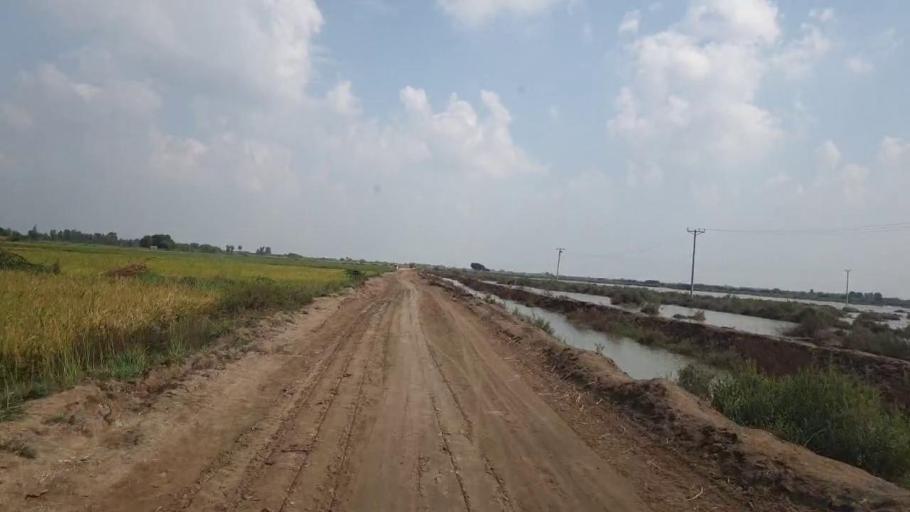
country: PK
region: Sindh
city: Badin
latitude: 24.5328
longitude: 68.6295
